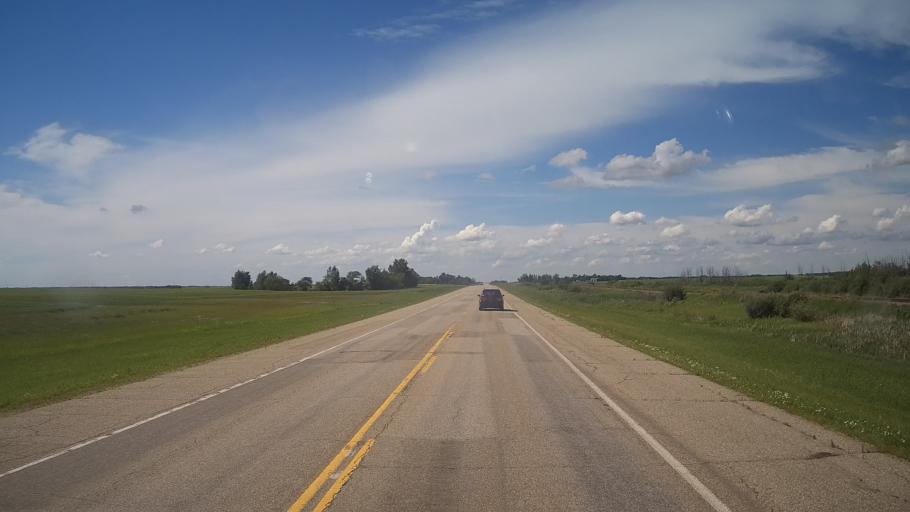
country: CA
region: Saskatchewan
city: Yorkton
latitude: 51.0836
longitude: -102.2502
